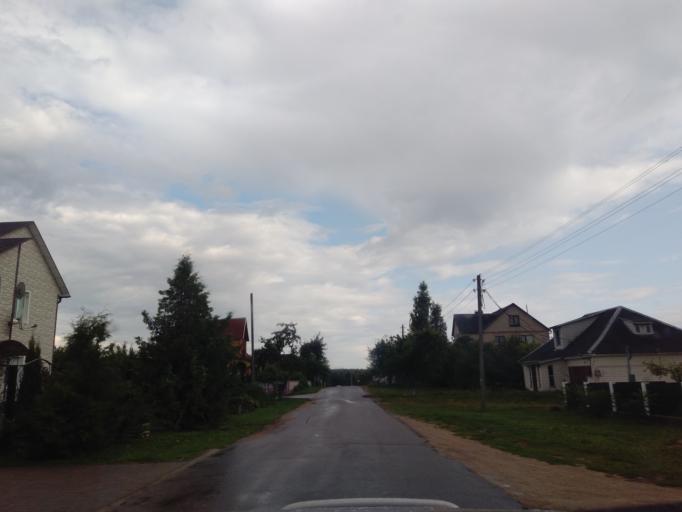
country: BY
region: Minsk
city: Kapyl'
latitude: 53.1657
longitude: 27.0886
